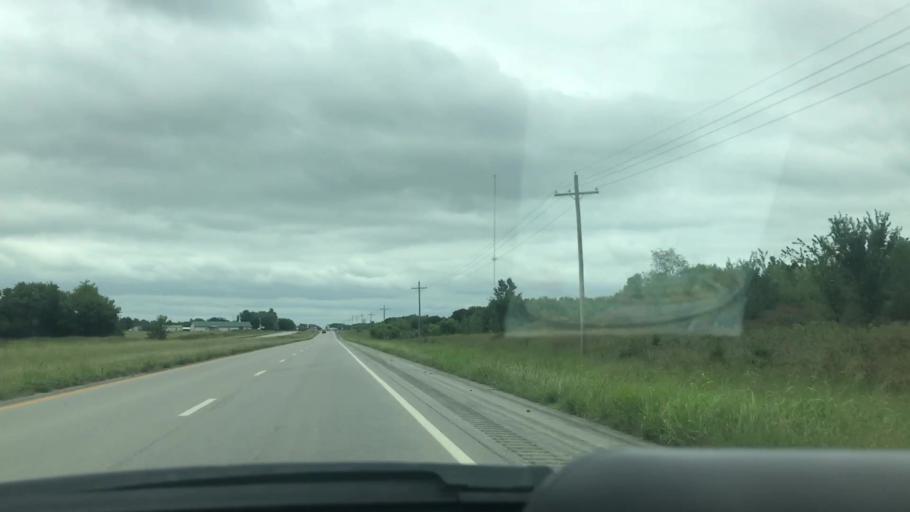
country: US
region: Oklahoma
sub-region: Mayes County
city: Pryor
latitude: 36.4184
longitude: -95.2784
